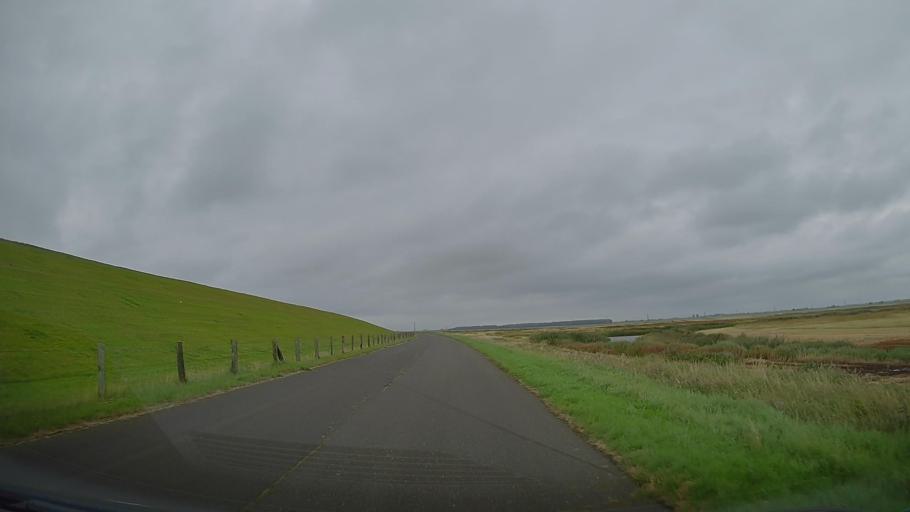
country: DE
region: Schleswig-Holstein
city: Busenwurth
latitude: 54.0408
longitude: 8.9785
